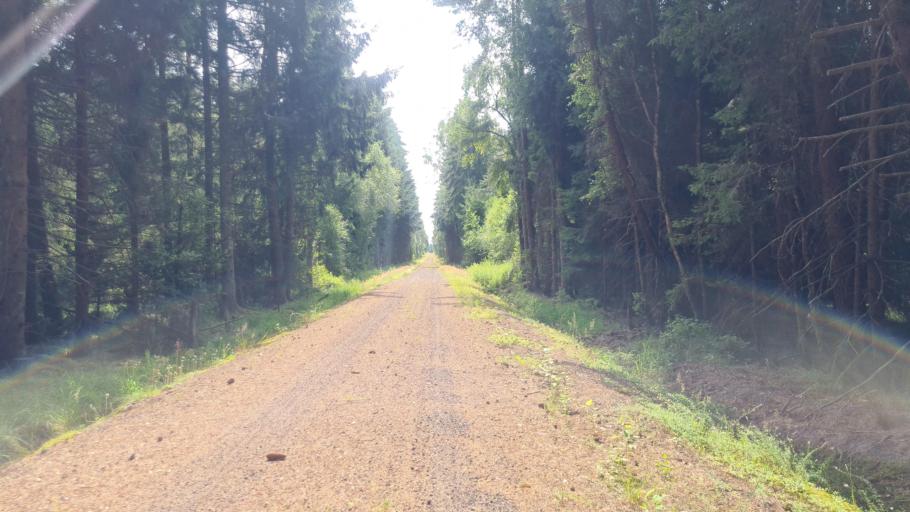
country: SE
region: Kronoberg
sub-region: Ljungby Kommun
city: Lagan
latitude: 56.9519
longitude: 13.9610
